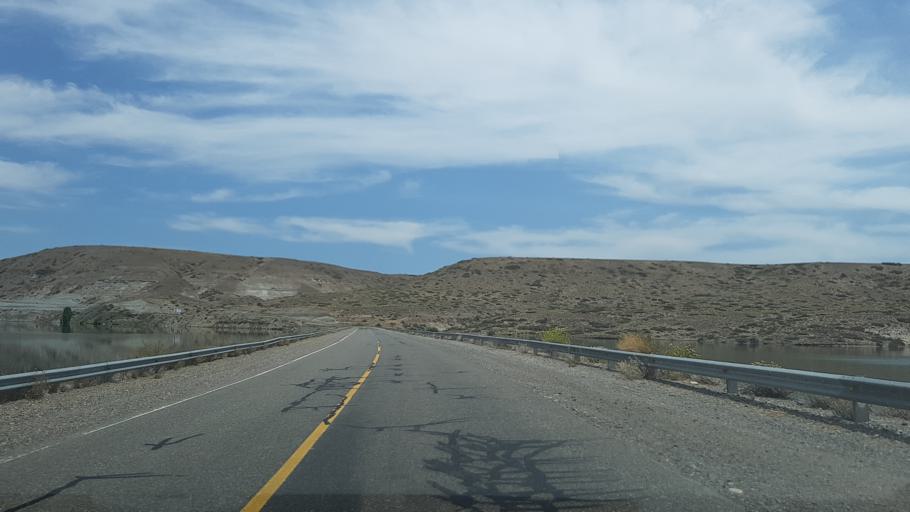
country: AR
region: Neuquen
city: Junin de los Andes
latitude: -40.4377
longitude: -70.6552
